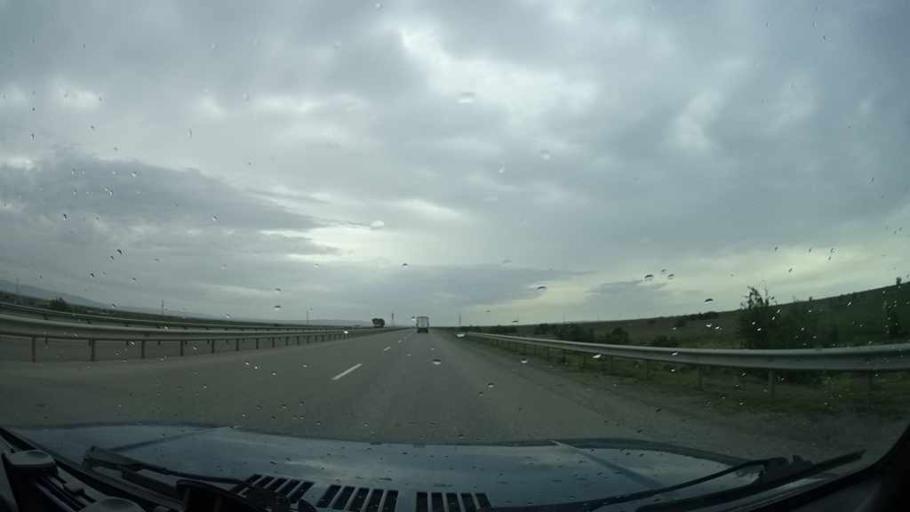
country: AZ
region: Goranboy
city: Goranboy
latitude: 40.6455
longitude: 46.7408
